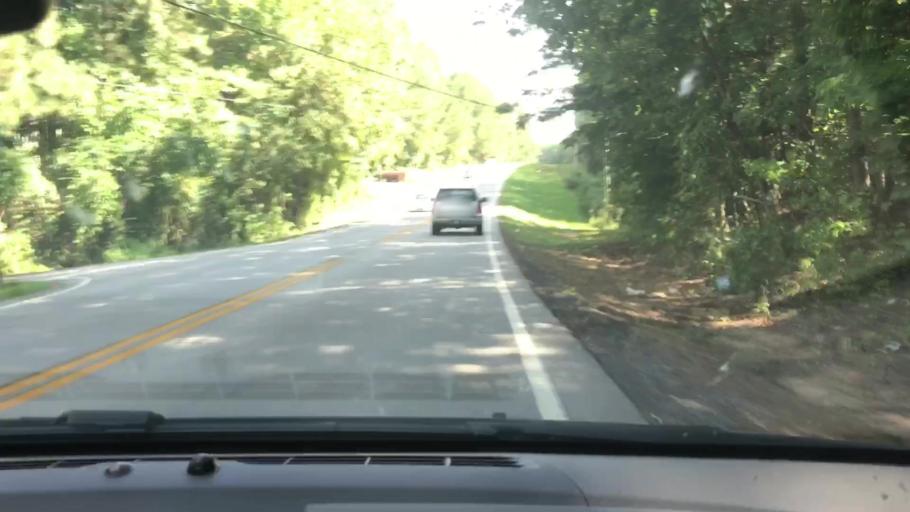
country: US
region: Georgia
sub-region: Troup County
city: La Grange
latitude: 33.0808
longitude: -85.0498
